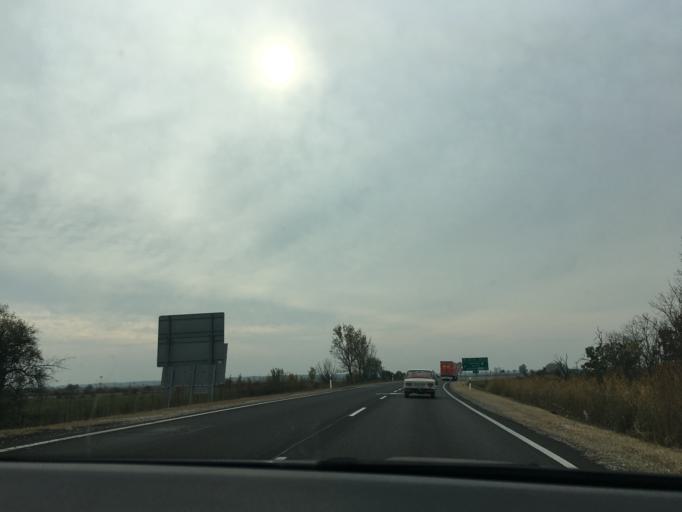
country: HU
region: Jasz-Nagykun-Szolnok
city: Kisujszallas
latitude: 47.2328
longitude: 20.8198
